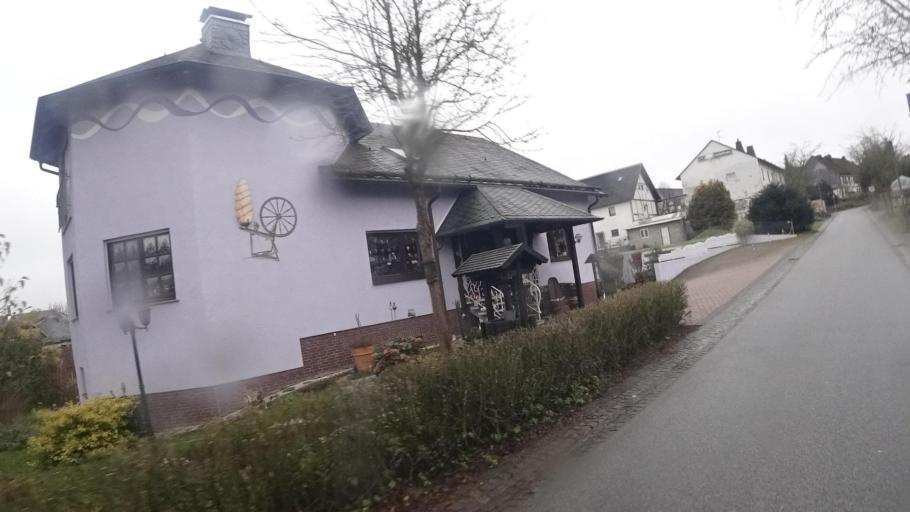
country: DE
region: Rheinland-Pfalz
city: Maisborn
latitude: 50.0777
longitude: 7.6026
